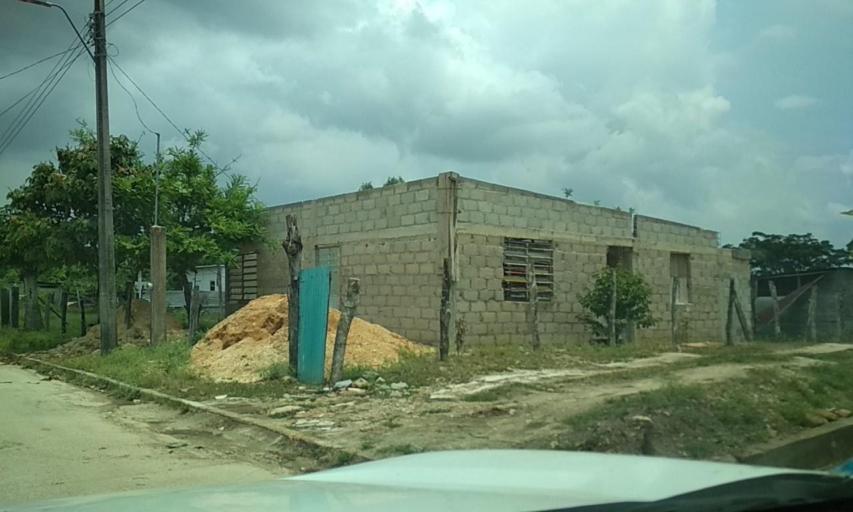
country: MX
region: Veracruz
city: Las Choapas
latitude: 17.8919
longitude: -94.0968
